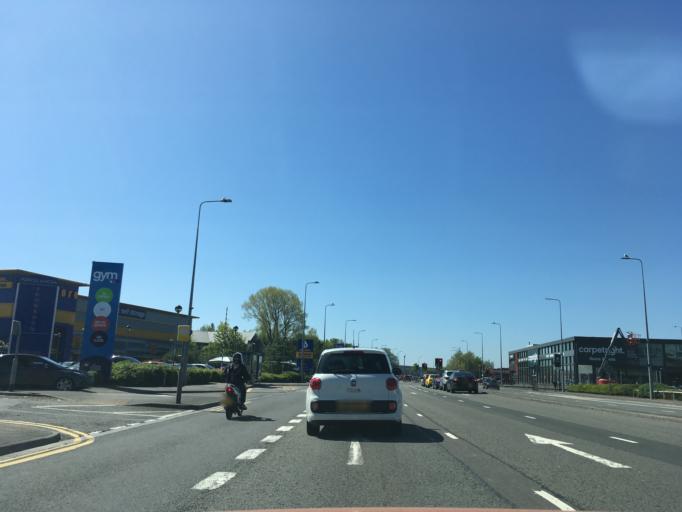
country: GB
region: Wales
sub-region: Cardiff
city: Cardiff
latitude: 51.4963
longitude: -3.1424
